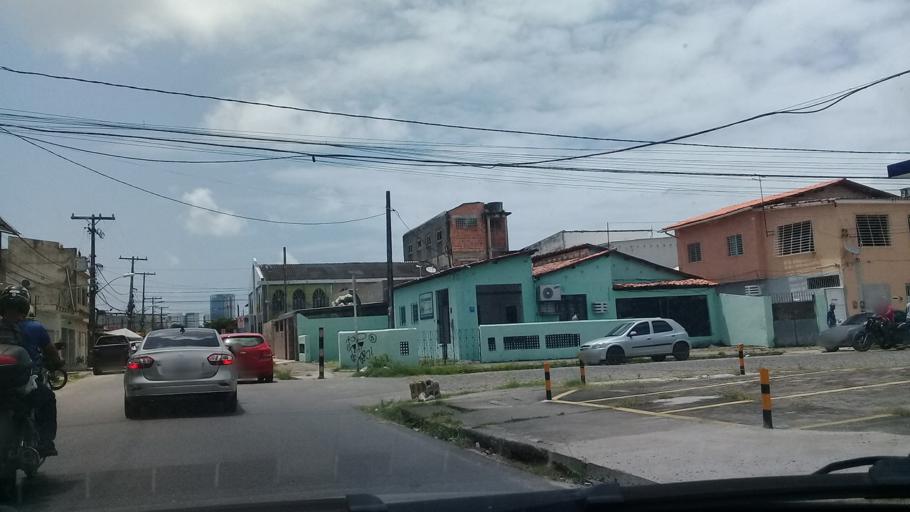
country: BR
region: Pernambuco
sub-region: Recife
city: Recife
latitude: -8.1058
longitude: -34.9192
